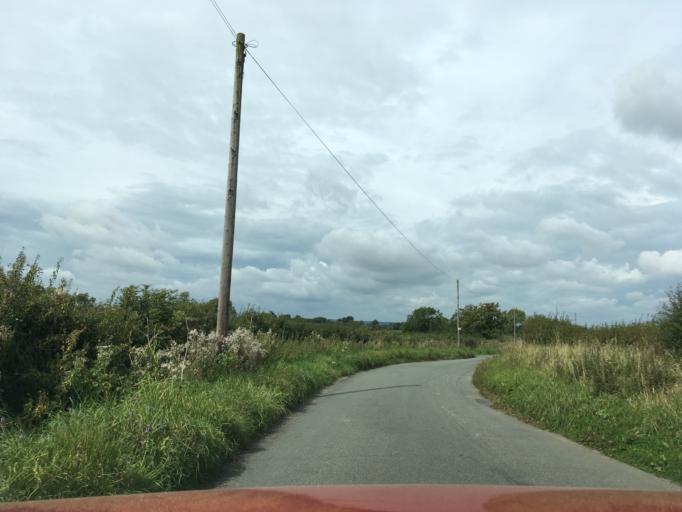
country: GB
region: England
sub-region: South Gloucestershire
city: Thornbury
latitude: 51.6161
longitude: -2.5554
